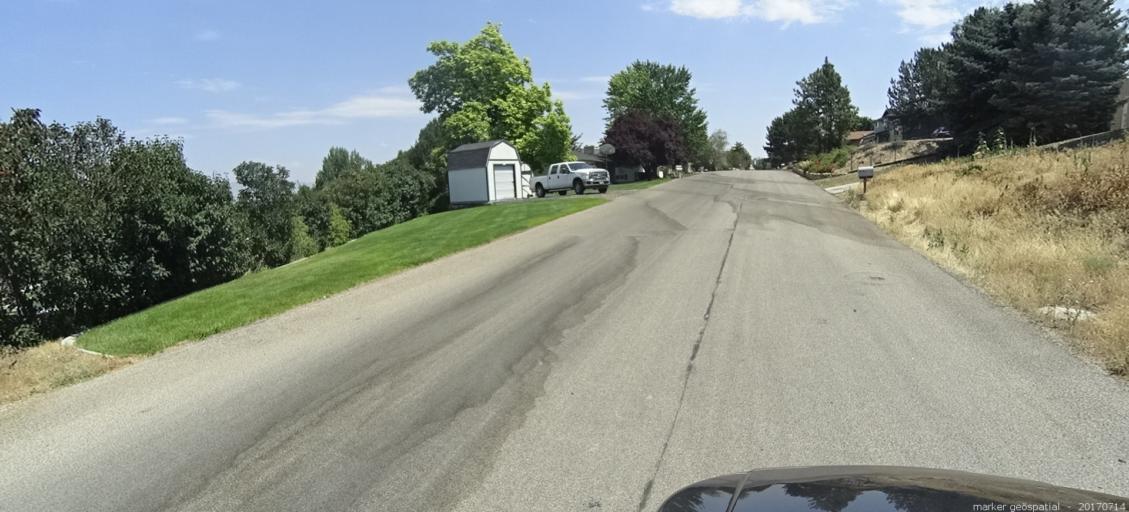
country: US
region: Idaho
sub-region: Ada County
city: Meridian
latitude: 43.5392
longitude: -116.3288
